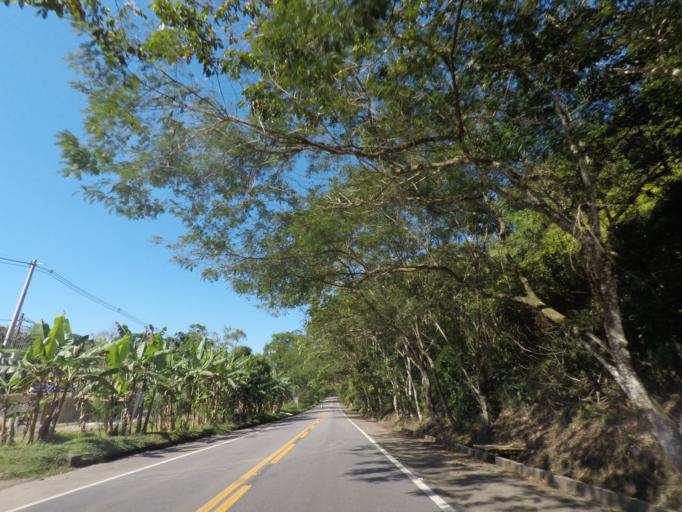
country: BR
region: Rio de Janeiro
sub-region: Parati
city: Paraty
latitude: -23.2721
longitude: -44.6853
